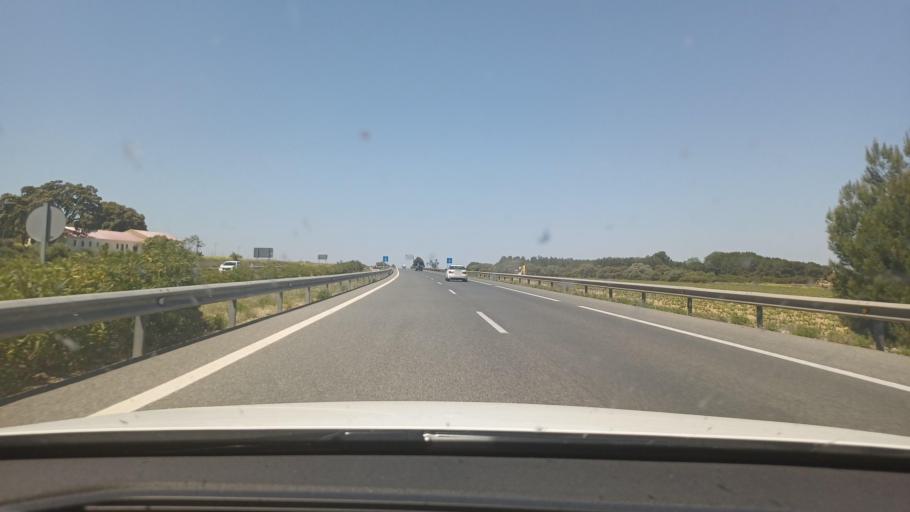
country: ES
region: Castille-La Mancha
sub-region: Provincia de Albacete
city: Corral-Rubio
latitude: 38.9006
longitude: -1.4758
